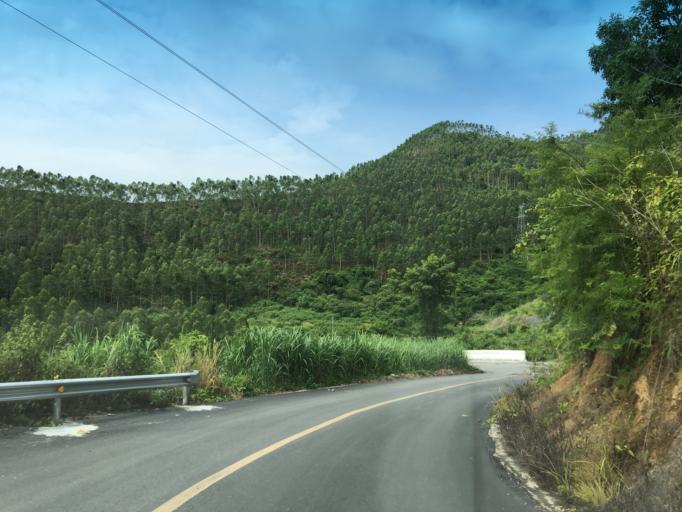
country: CN
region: Guangxi Zhuangzu Zizhiqu
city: Xinzhou
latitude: 24.8184
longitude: 105.6466
